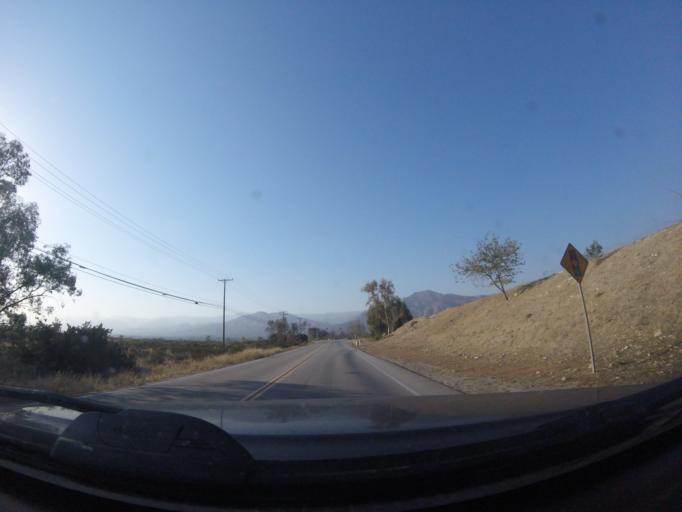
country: US
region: California
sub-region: San Bernardino County
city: Highland
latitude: 34.0971
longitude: -117.1824
